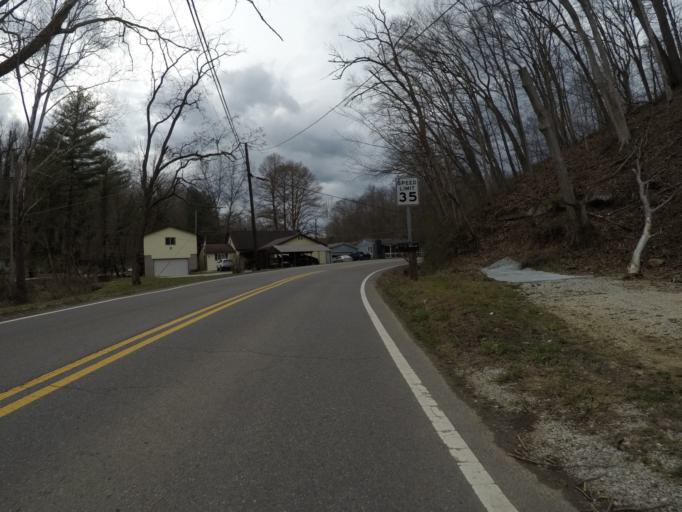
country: US
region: Ohio
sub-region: Lawrence County
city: Burlington
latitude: 38.4269
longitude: -82.5152
